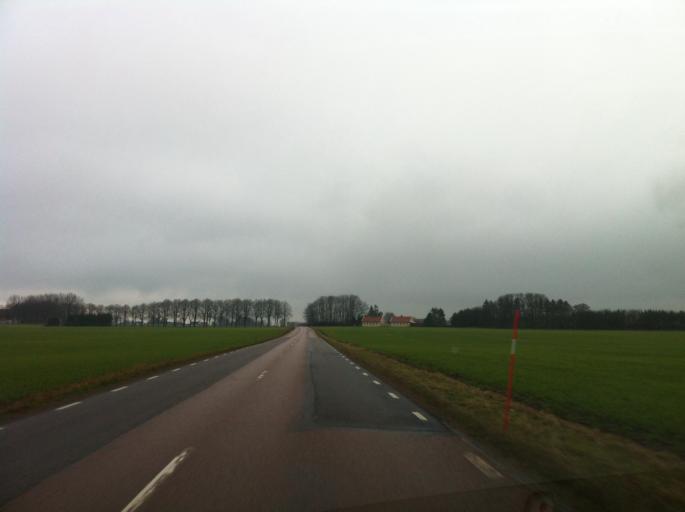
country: SE
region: Skane
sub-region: Helsingborg
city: Barslov
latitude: 55.9775
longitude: 12.8589
